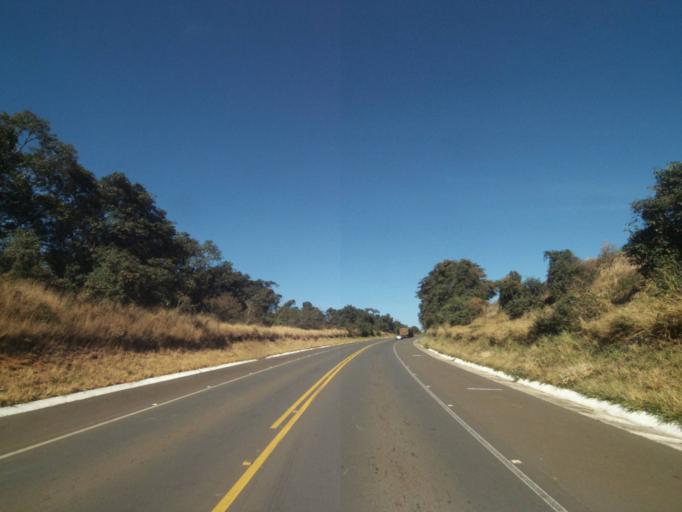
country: BR
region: Parana
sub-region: Tibagi
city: Tibagi
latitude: -24.7149
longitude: -50.4494
